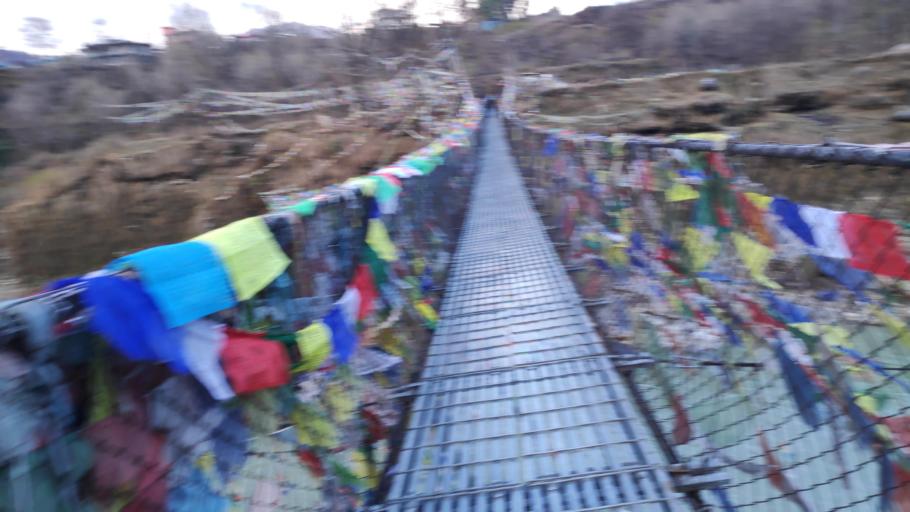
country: NP
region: Western Region
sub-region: Gandaki Zone
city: Pokhara
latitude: 28.2576
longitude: 83.9650
